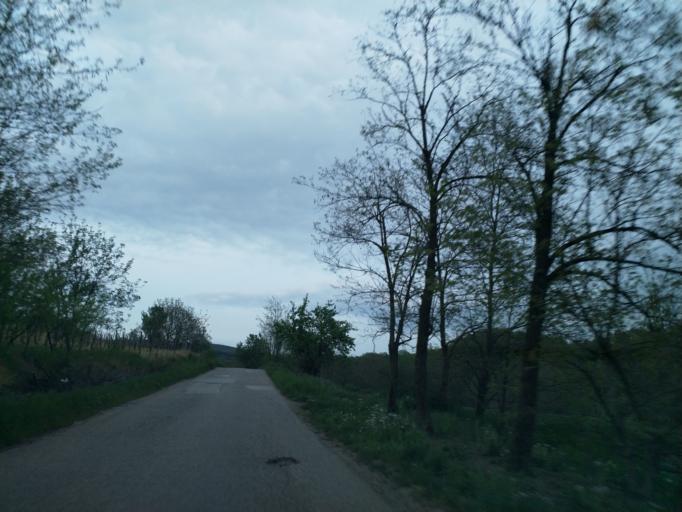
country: RS
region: Central Serbia
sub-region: Pomoravski Okrug
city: Cuprija
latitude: 43.9548
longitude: 21.4806
